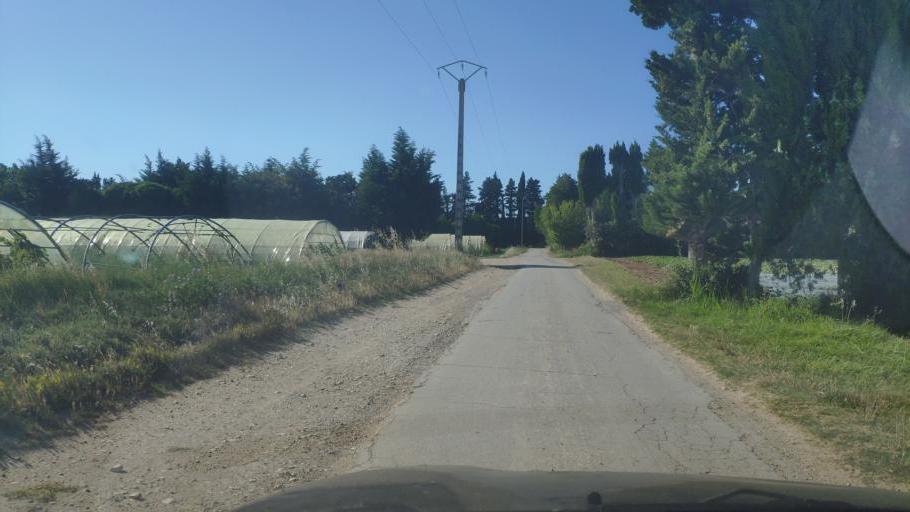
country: FR
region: Provence-Alpes-Cote d'Azur
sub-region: Departement du Vaucluse
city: Aubignan
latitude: 44.0800
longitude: 5.0210
